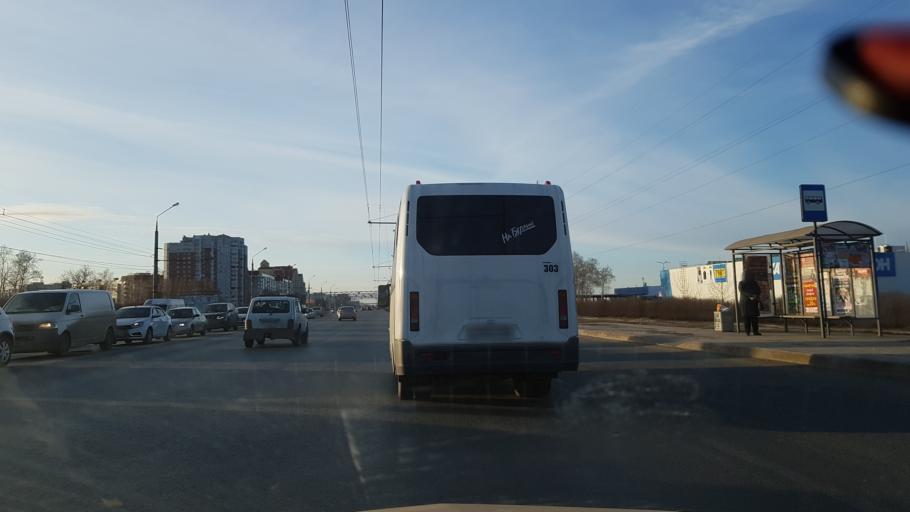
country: RU
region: Samara
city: Tol'yatti
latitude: 53.5454
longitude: 49.3785
